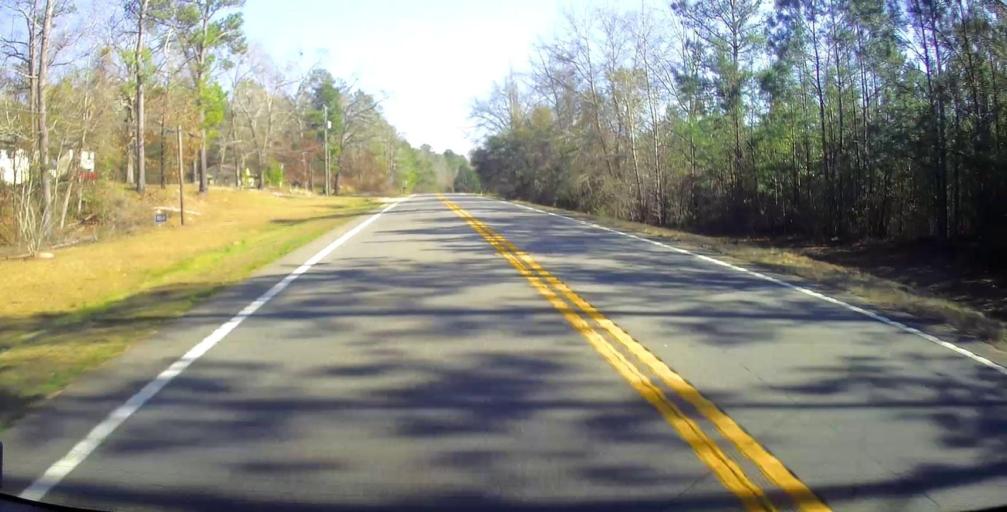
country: US
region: Georgia
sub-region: Macon County
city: Oglethorpe
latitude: 32.3653
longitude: -84.1849
